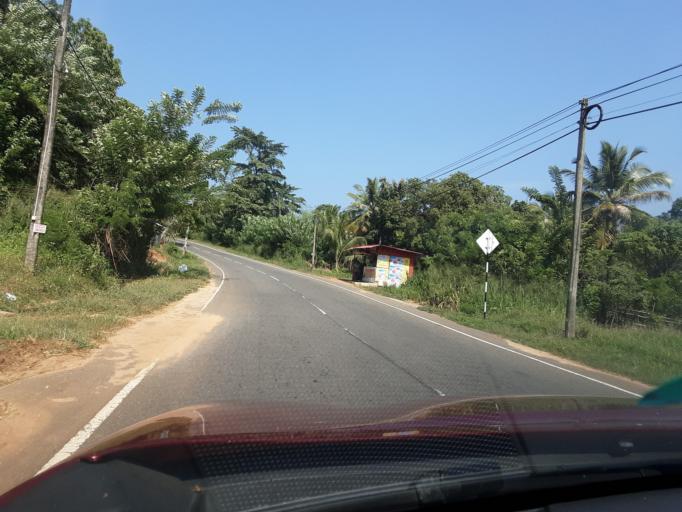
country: LK
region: Uva
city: Badulla
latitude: 7.1822
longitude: 81.0463
